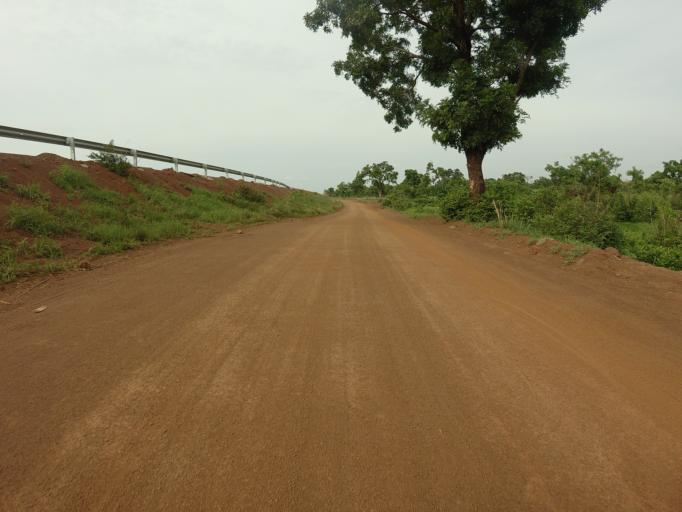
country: GH
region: Northern
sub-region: Yendi
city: Yendi
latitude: 9.7922
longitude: -0.1151
